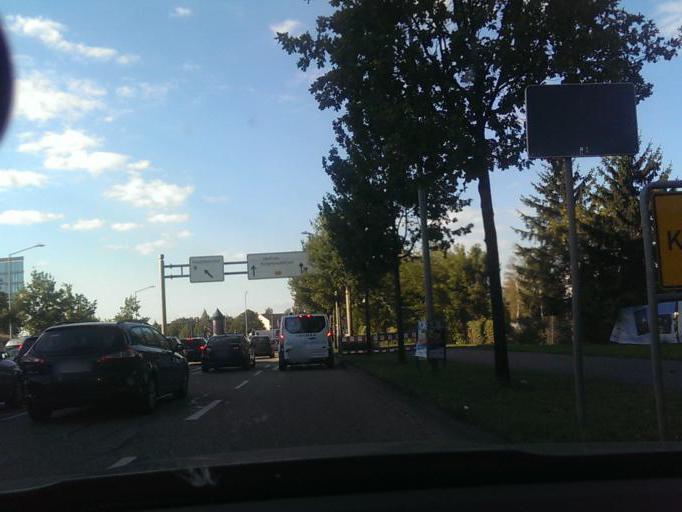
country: DE
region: Baden-Wuerttemberg
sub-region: Karlsruhe Region
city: Karlsruhe
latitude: 49.0020
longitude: 8.4256
